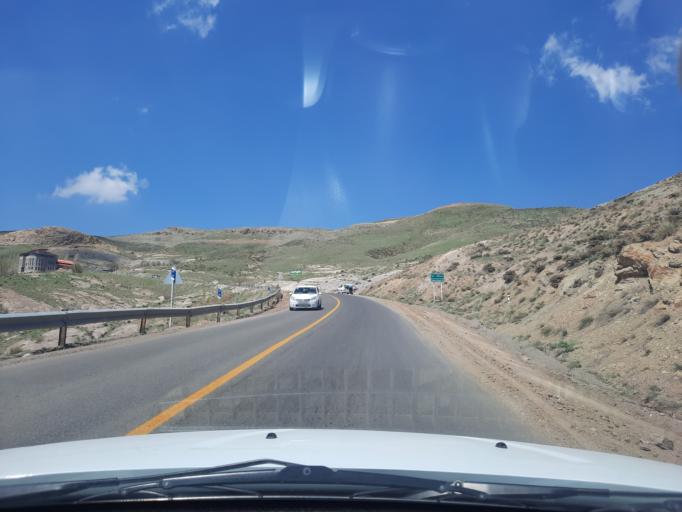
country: IR
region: Qazvin
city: Qazvin
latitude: 36.3776
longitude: 50.2103
